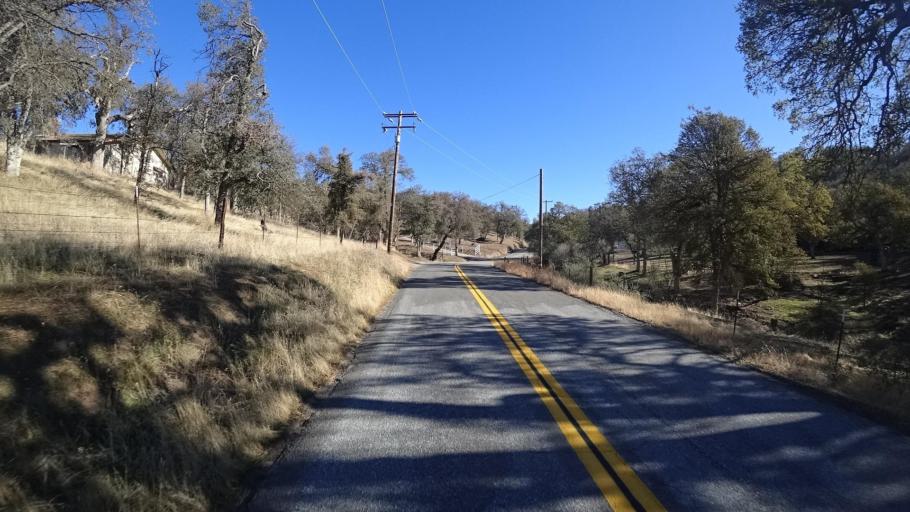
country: US
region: California
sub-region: Kern County
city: Alta Sierra
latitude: 35.7911
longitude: -118.7365
